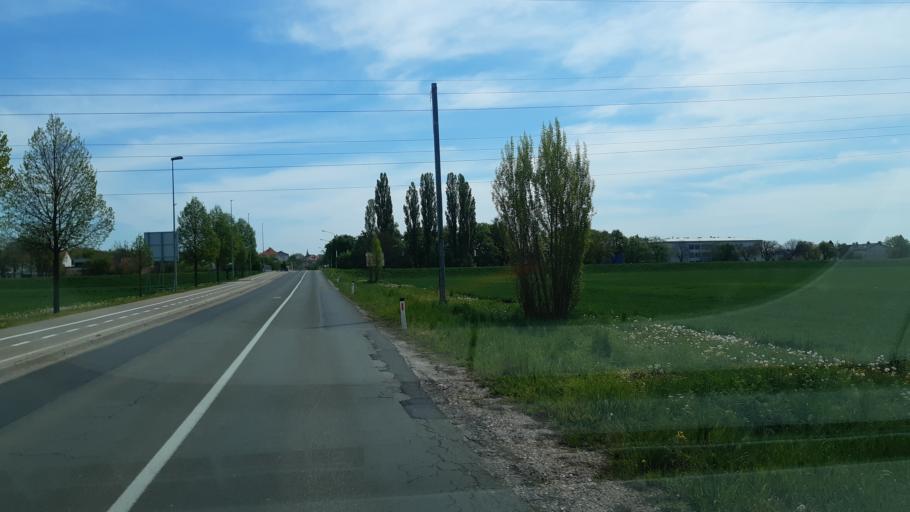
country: SI
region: Murska Sobota
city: Cernelavci
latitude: 46.6622
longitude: 16.1480
